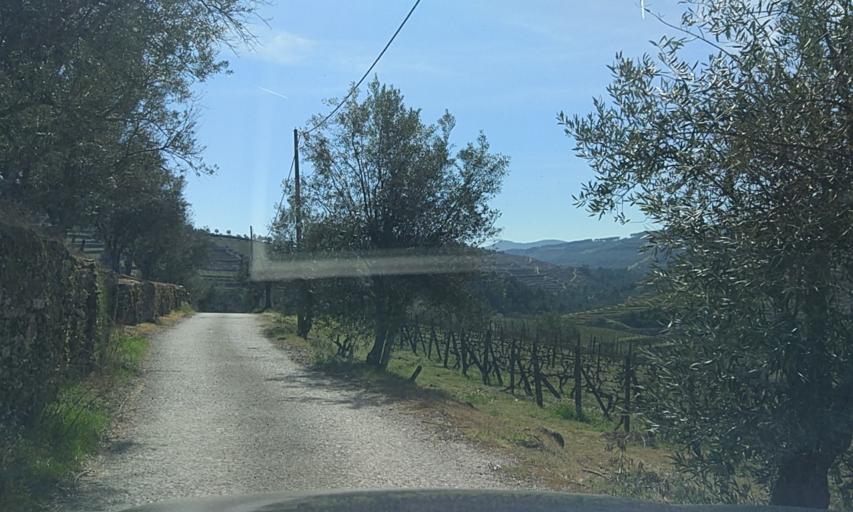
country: PT
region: Vila Real
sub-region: Sabrosa
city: Sabrosa
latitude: 41.3070
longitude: -7.5494
